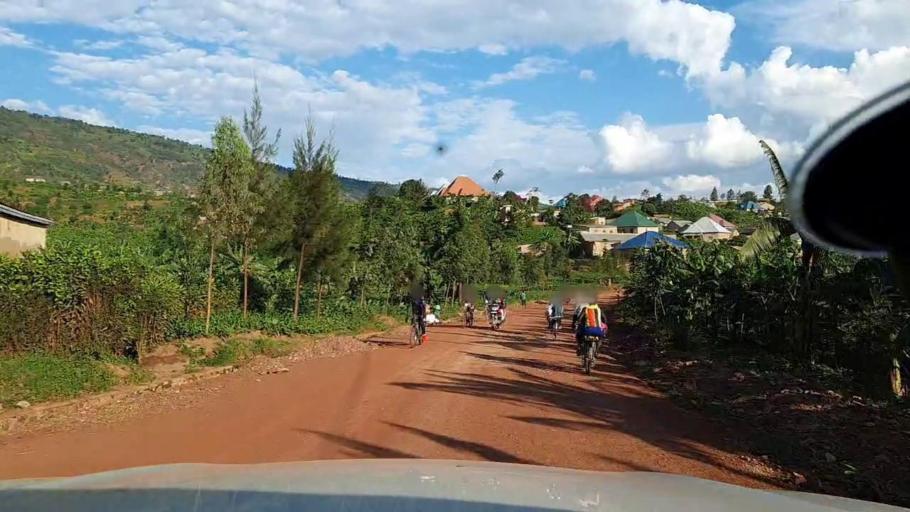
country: RW
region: Kigali
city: Kigali
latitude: -1.8945
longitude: 29.9637
